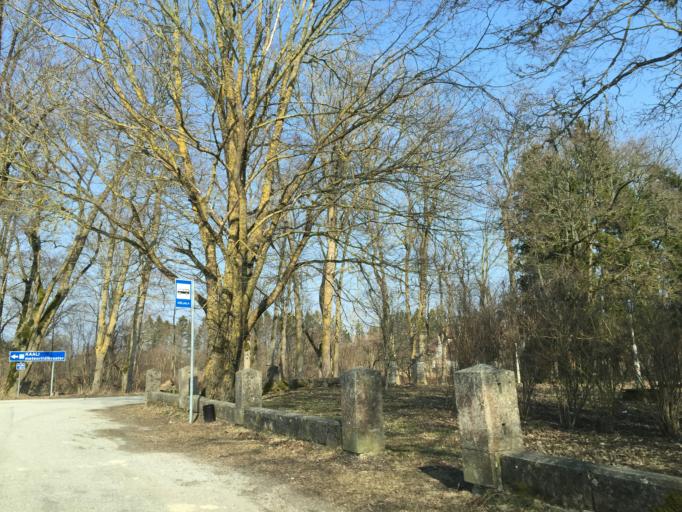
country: EE
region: Saare
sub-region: Kuressaare linn
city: Kuressaare
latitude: 58.3702
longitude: 22.6845
